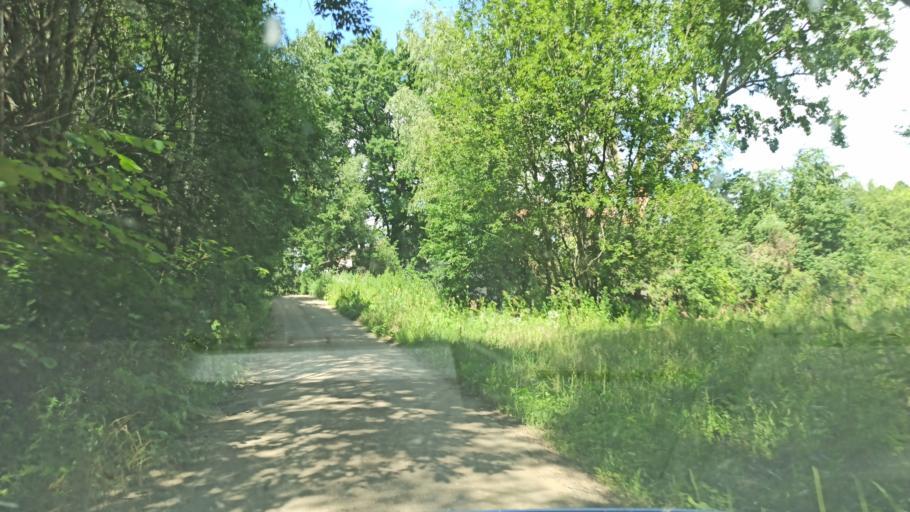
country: PL
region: Warmian-Masurian Voivodeship
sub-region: Powiat ostrodzki
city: Milakowo
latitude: 53.8583
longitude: 20.0658
